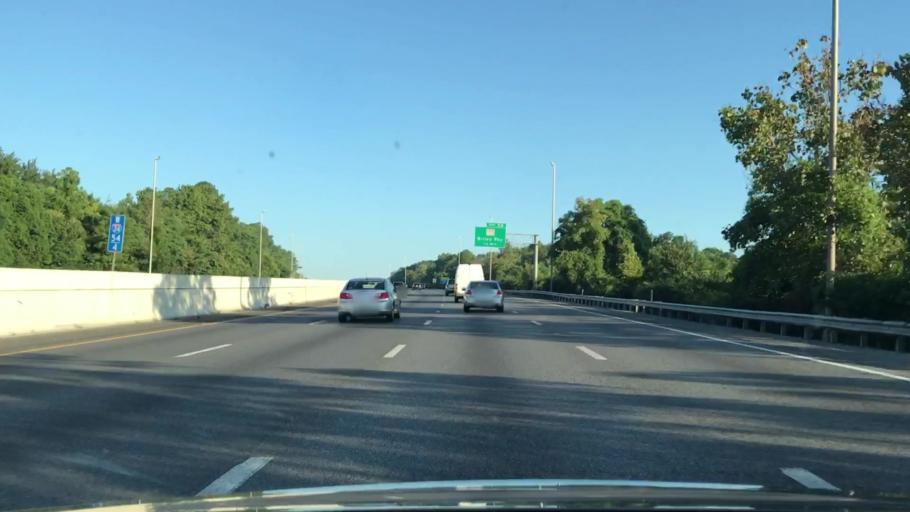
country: US
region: Tennessee
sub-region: Davidson County
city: Oak Hill
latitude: 36.1150
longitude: -86.7290
